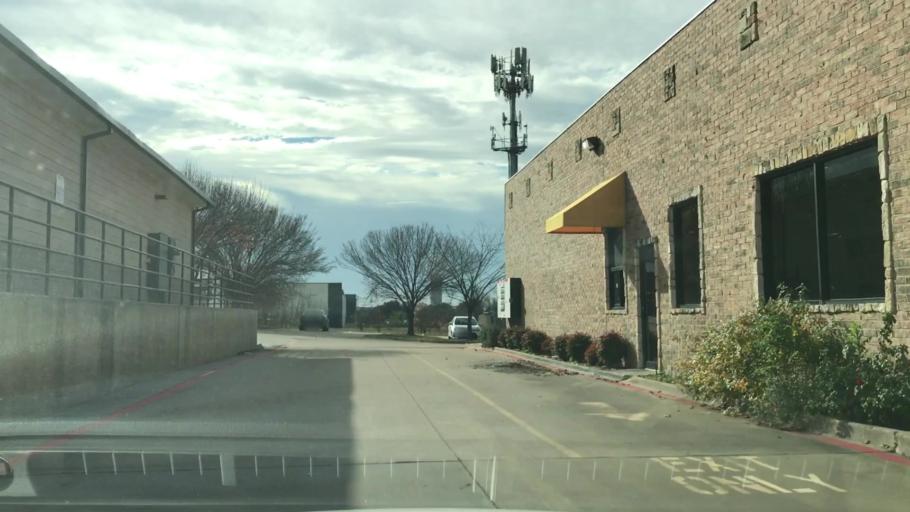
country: US
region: Texas
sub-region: Dallas County
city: Coppell
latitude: 32.9202
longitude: -96.9947
